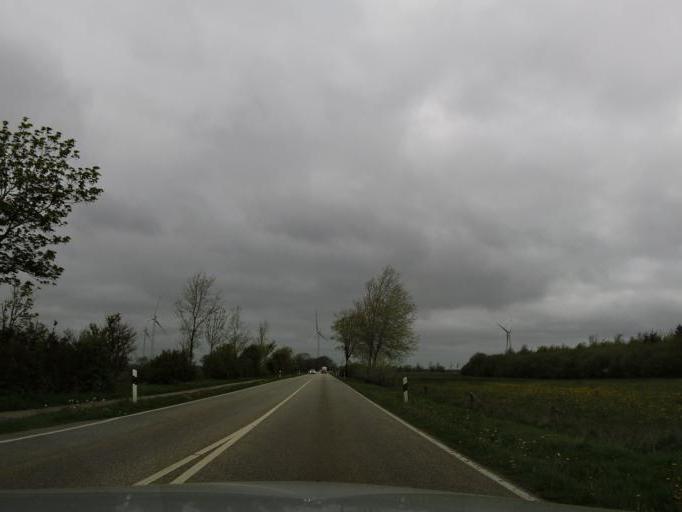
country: DE
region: Schleswig-Holstein
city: Suderlugum
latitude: 54.8846
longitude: 8.9086
